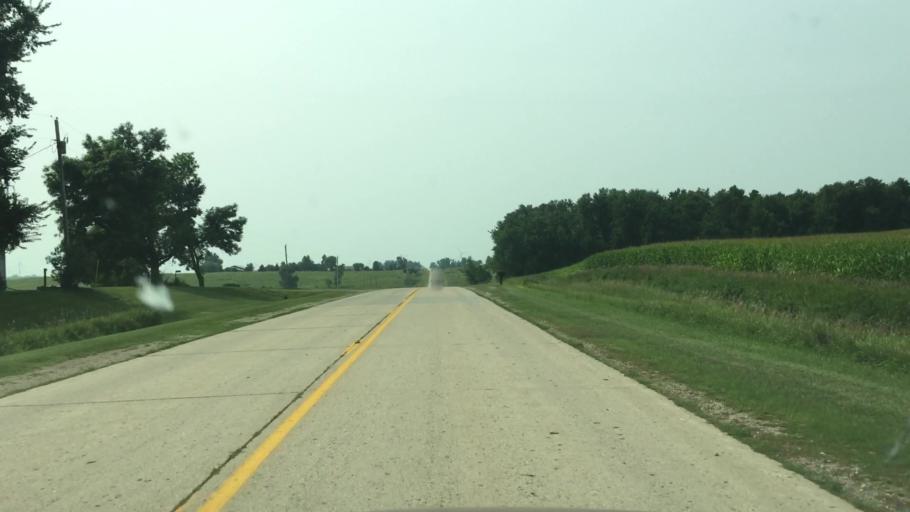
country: US
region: Iowa
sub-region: Dickinson County
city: Lake Park
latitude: 43.4212
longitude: -95.2891
